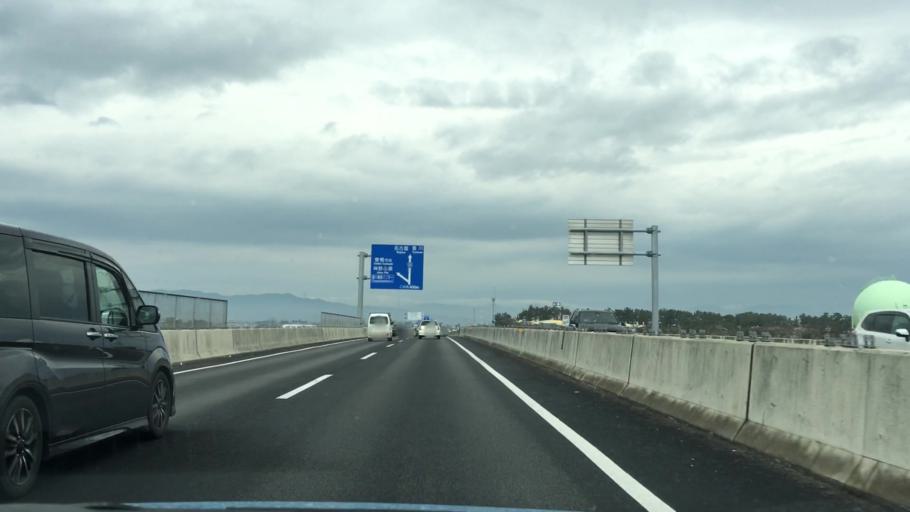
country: JP
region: Aichi
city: Toyohashi
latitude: 34.7535
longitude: 137.3346
